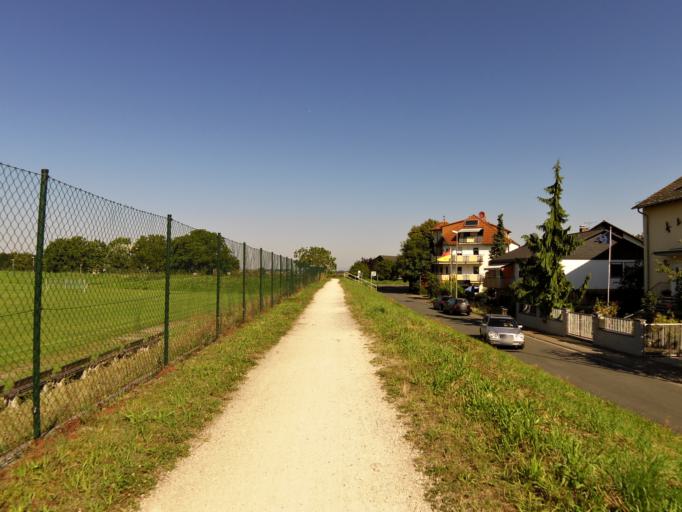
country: DE
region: Hesse
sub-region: Regierungsbezirk Darmstadt
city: Stockstadt am Rhein
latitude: 49.8381
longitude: 8.4610
